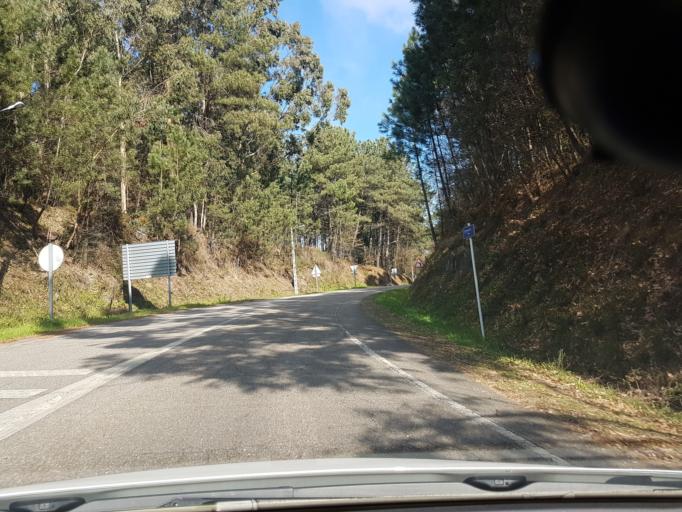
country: ES
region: Galicia
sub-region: Provincia de Pontevedra
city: Porrino
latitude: 42.2087
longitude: -8.6438
